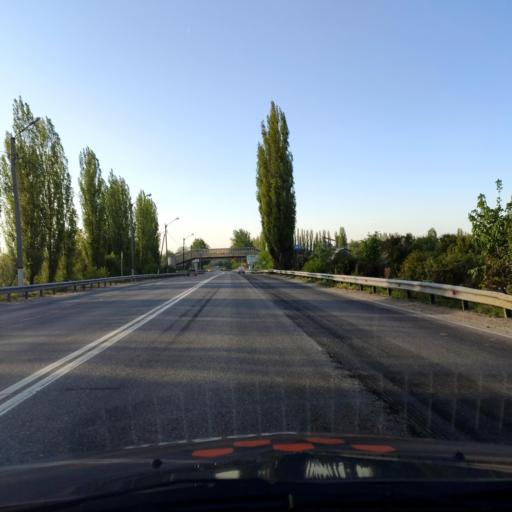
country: RU
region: Lipetsk
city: Yelets
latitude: 52.6017
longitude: 38.4715
